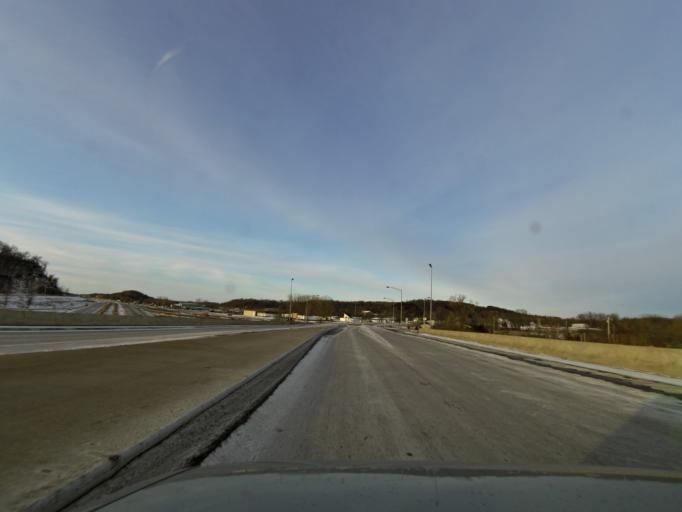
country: US
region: Wisconsin
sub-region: Pierce County
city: River Falls
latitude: 44.8790
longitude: -92.6225
